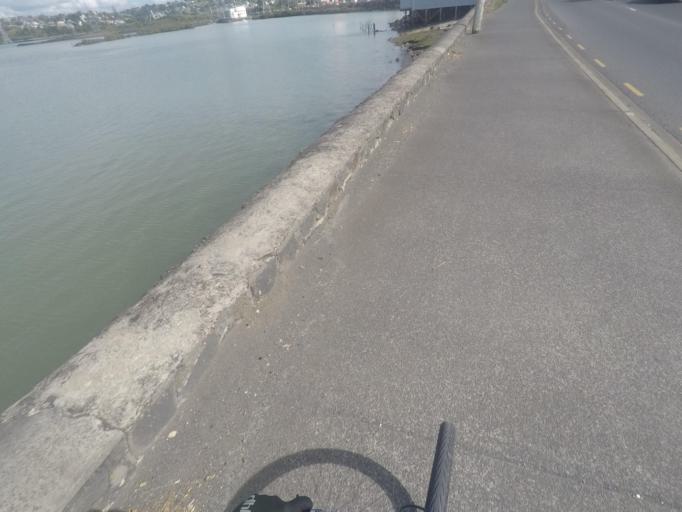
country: NZ
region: Auckland
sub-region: Auckland
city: Mangere
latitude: -36.9304
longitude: 174.7821
